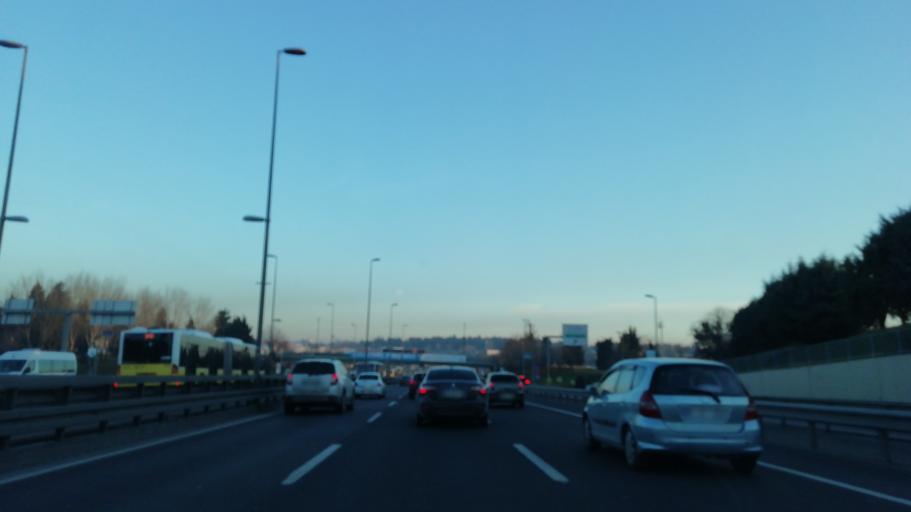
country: TR
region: Istanbul
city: Istanbul
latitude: 41.0262
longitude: 28.9231
